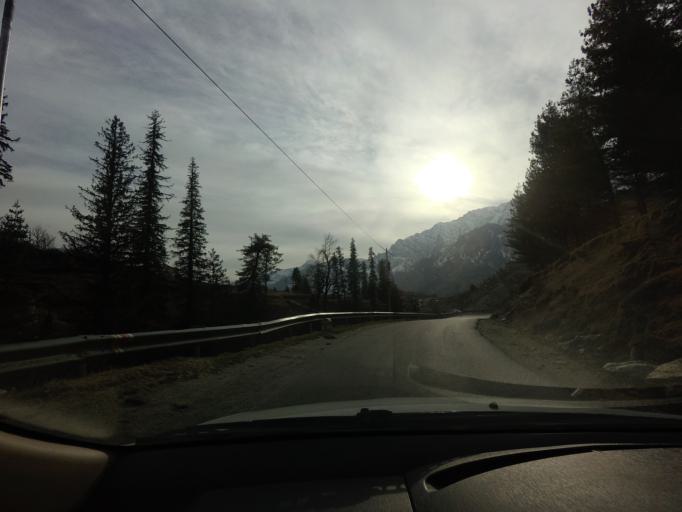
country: IN
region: Himachal Pradesh
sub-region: Kulu
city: Manali
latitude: 32.3157
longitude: 77.1849
